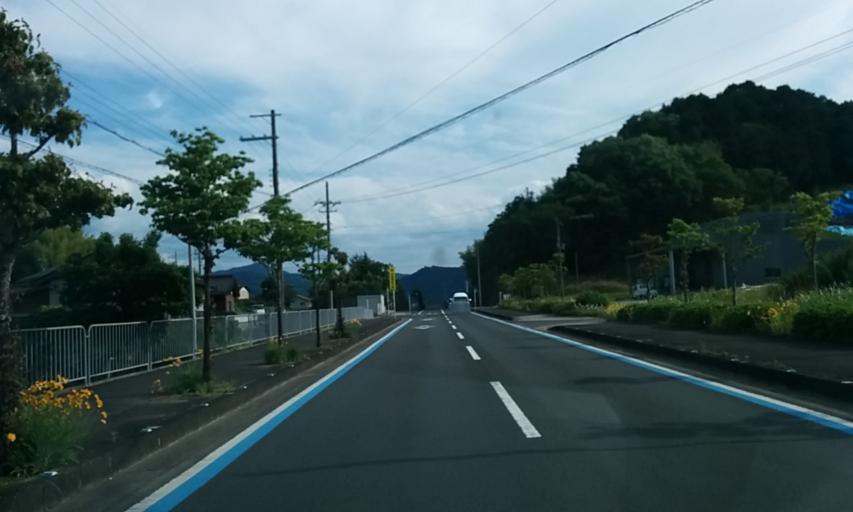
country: JP
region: Kyoto
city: Ayabe
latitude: 35.3176
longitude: 135.2607
